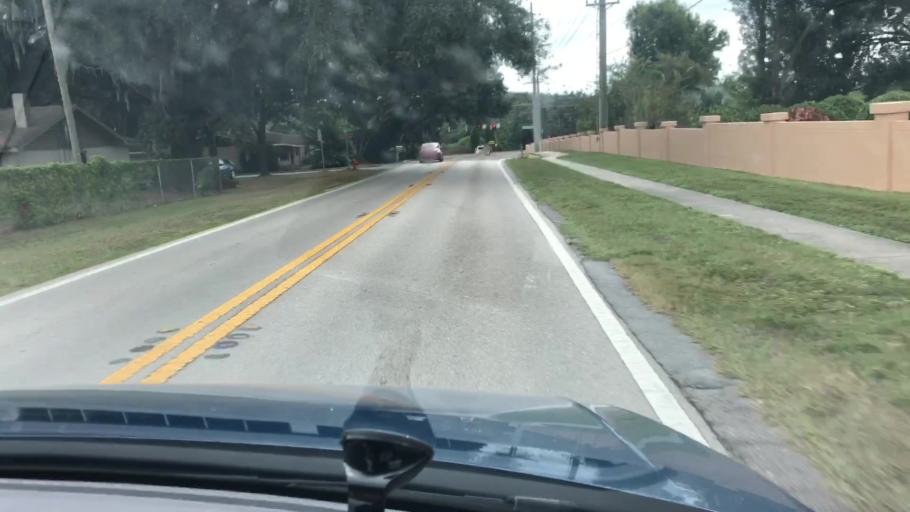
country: US
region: Florida
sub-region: Polk County
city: Gibsonia
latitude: 28.1284
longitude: -81.9403
